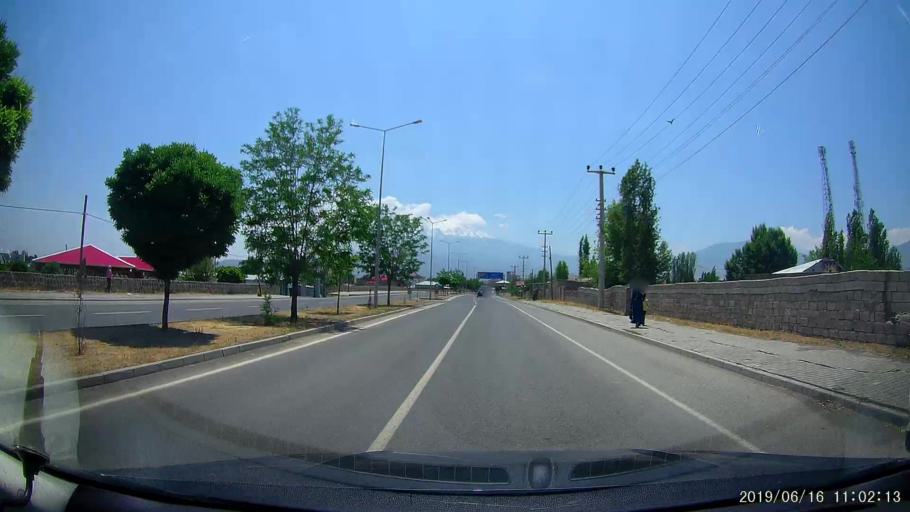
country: TR
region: Igdir
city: Igdir
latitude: 39.9085
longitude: 44.0577
